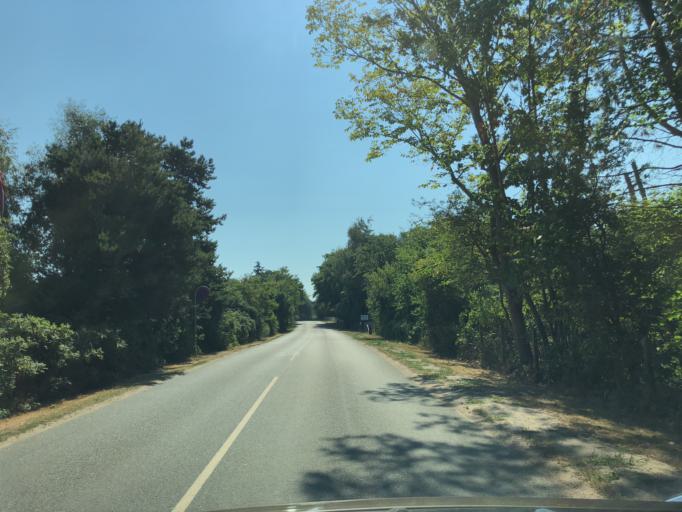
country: DK
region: Zealand
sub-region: Odsherred Kommune
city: Asnaes
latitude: 55.9828
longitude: 11.3080
